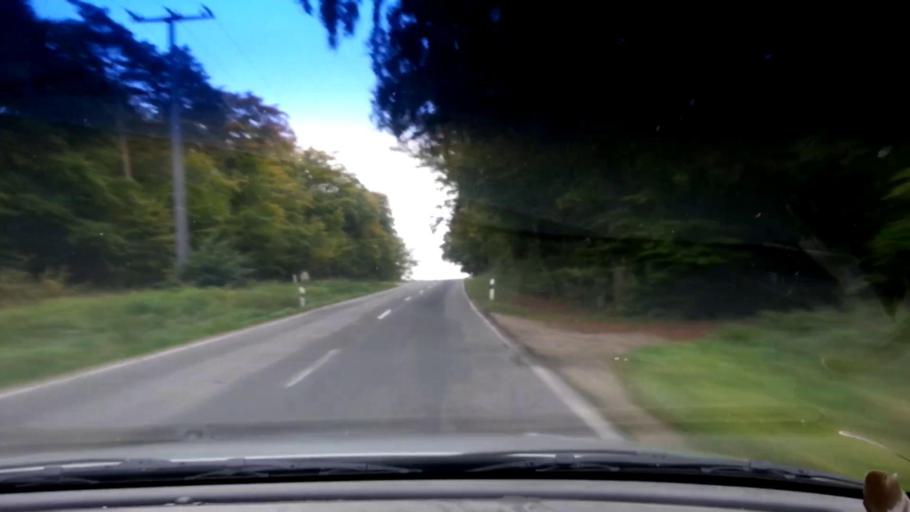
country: DE
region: Bavaria
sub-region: Upper Franconia
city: Priesendorf
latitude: 49.8980
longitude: 10.6555
